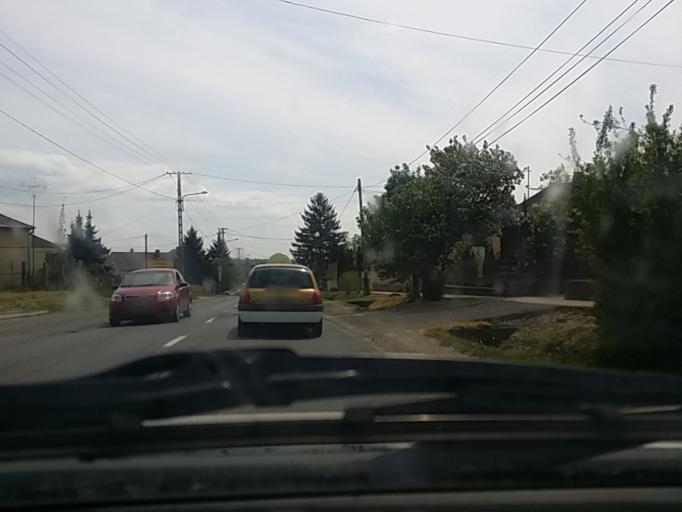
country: HU
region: Zala
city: Nagykanizsa
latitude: 46.4465
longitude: 17.0288
